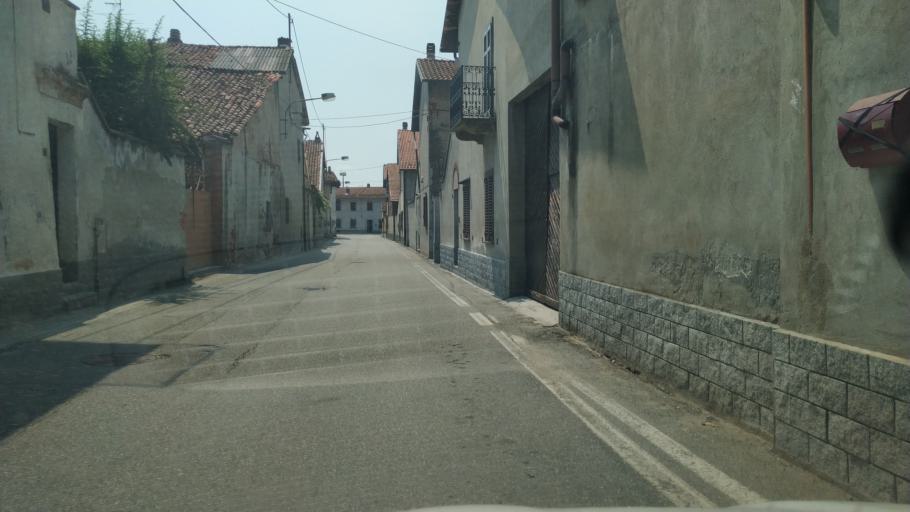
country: IT
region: Piedmont
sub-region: Provincia di Torino
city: Rondissone
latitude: 45.2458
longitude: 7.9660
